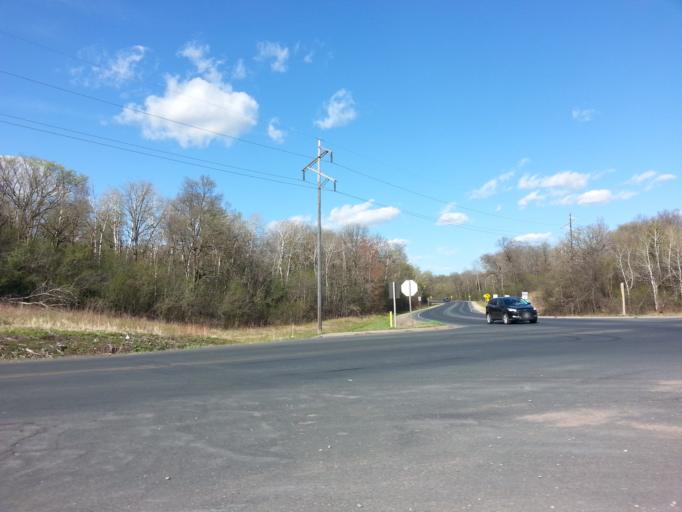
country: US
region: Wisconsin
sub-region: Saint Croix County
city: Somerset
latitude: 45.0350
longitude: -92.6691
